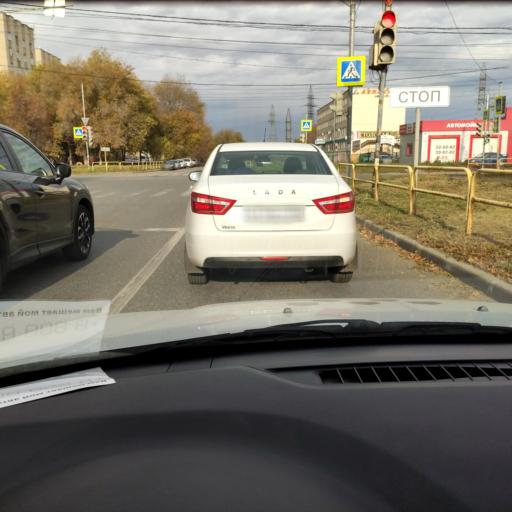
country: RU
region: Samara
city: Tol'yatti
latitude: 53.5397
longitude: 49.4093
